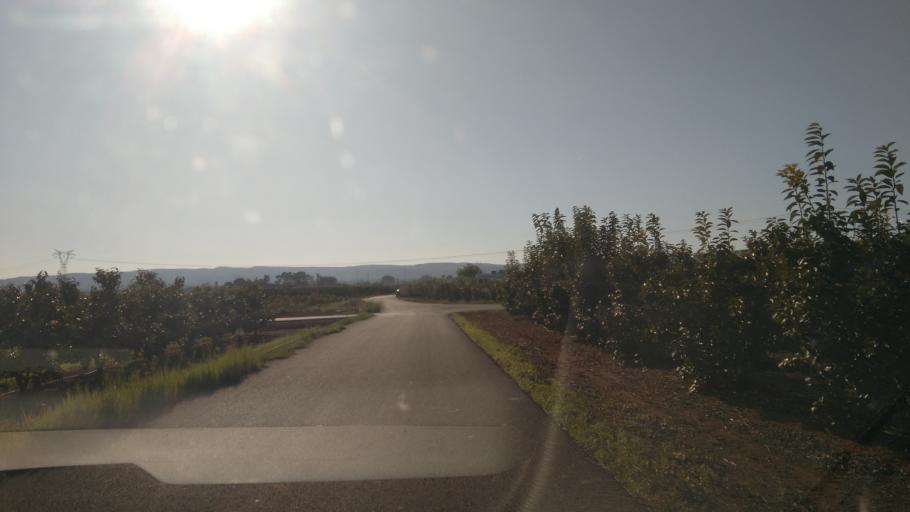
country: ES
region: Valencia
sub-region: Provincia de Valencia
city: Masalaves
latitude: 39.1782
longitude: -0.5376
